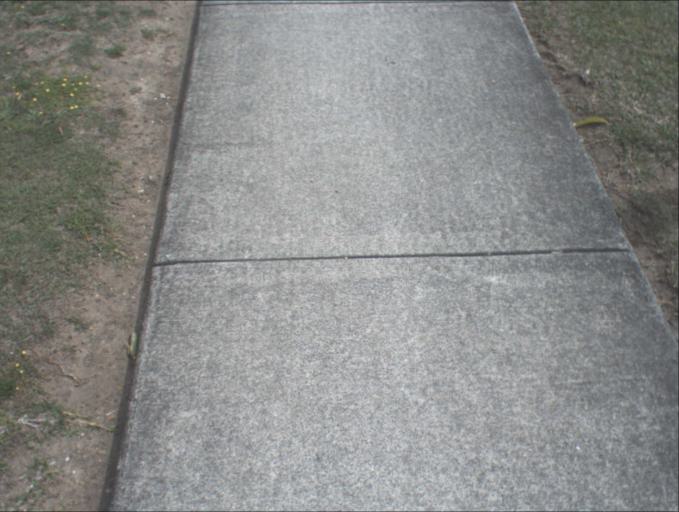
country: AU
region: Queensland
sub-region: Logan
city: Logan City
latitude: -27.6699
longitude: 153.0854
